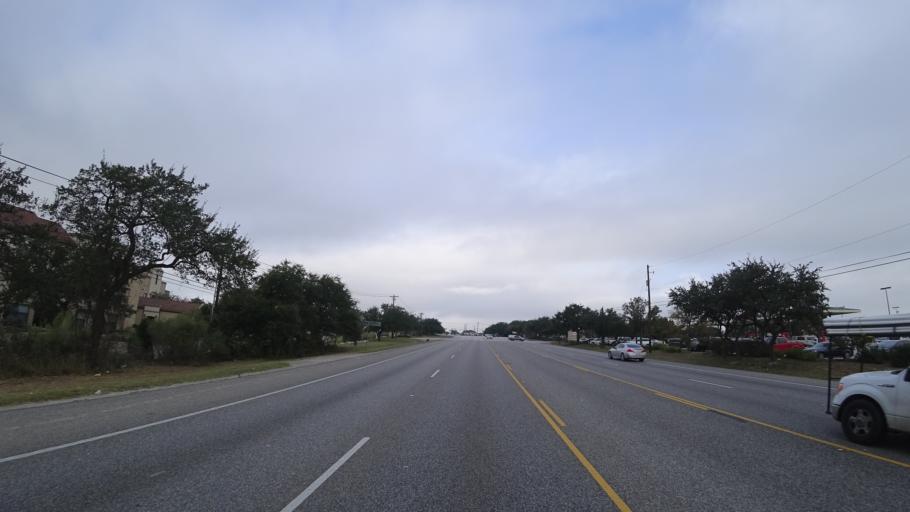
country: US
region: Texas
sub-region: Travis County
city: Bee Cave
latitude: 30.3029
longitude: -97.9326
